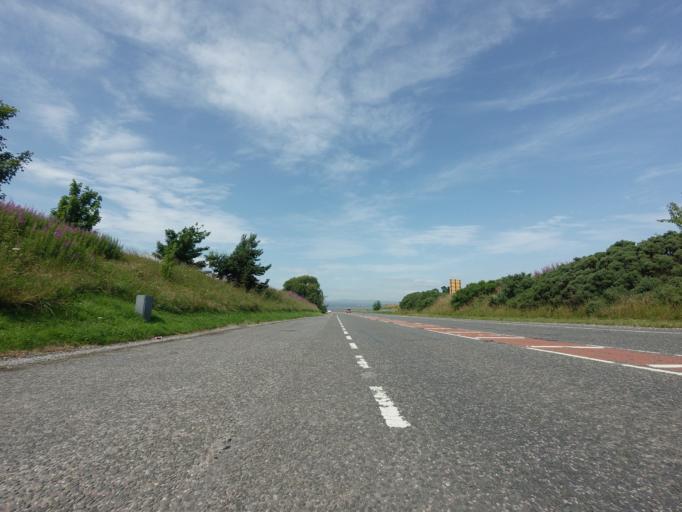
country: GB
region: Scotland
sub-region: Highland
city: Tain
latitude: 57.8257
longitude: -4.0797
